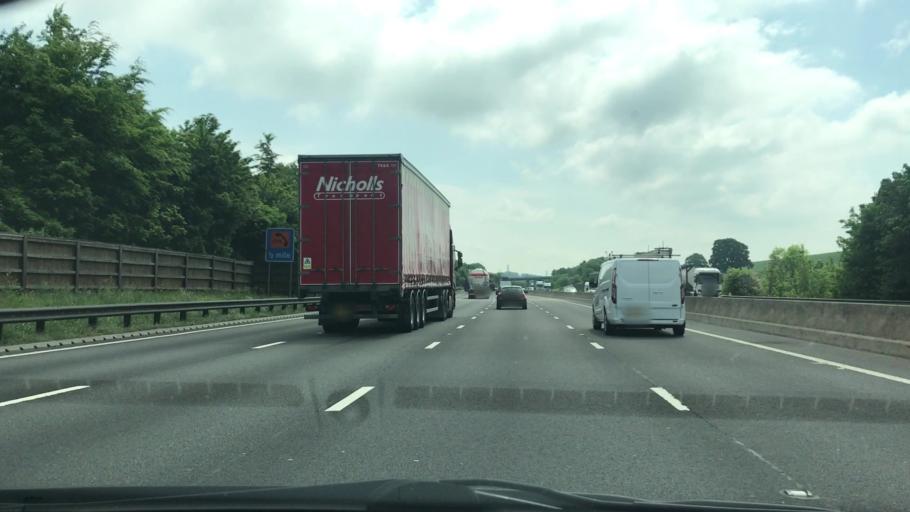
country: GB
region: England
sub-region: Derbyshire
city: Tibshelf
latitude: 53.1712
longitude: -1.3245
